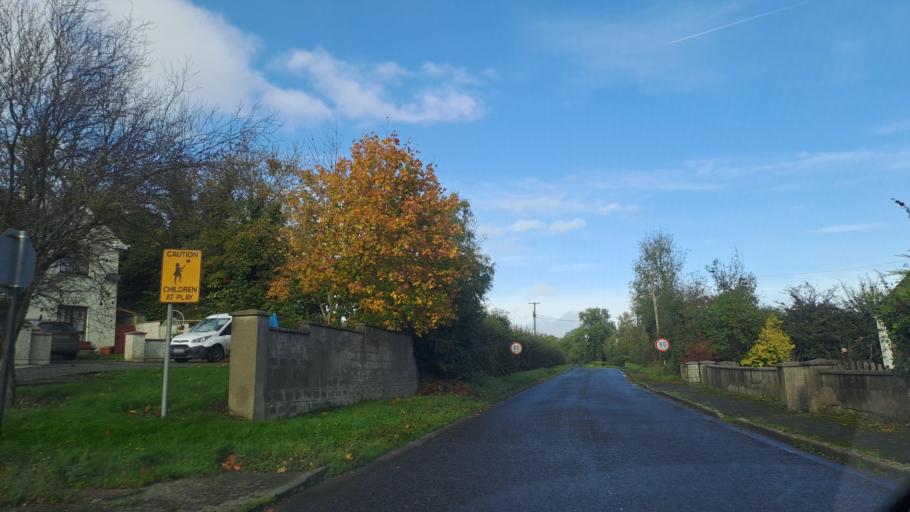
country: IE
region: Leinster
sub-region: Lu
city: Ardee
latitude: 53.8538
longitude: -6.6577
